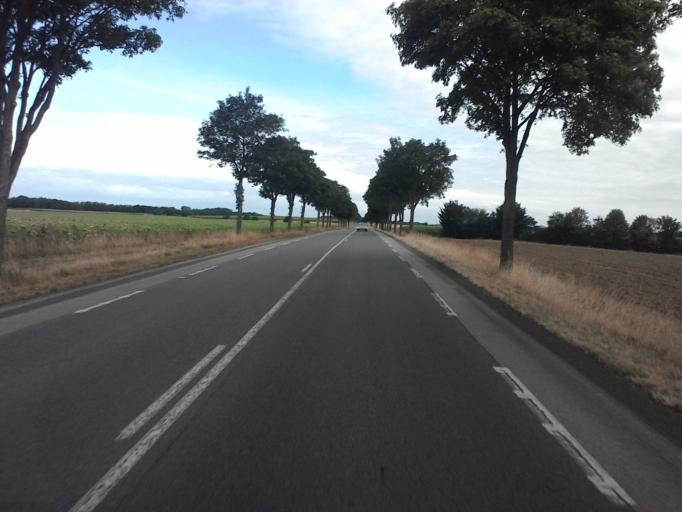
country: FR
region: Rhone-Alpes
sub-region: Departement de l'Ain
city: Saint-Martin-du-Mont
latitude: 46.1064
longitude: 5.3054
